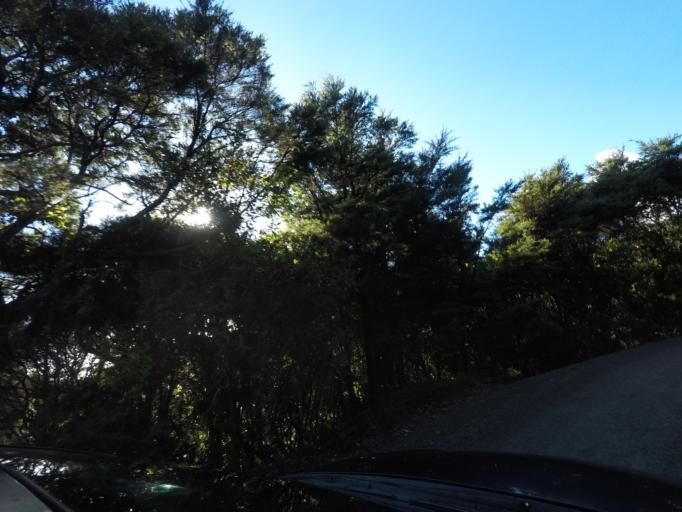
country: NZ
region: Auckland
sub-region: Auckland
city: Titirangi
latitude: -37.0145
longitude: 174.6036
